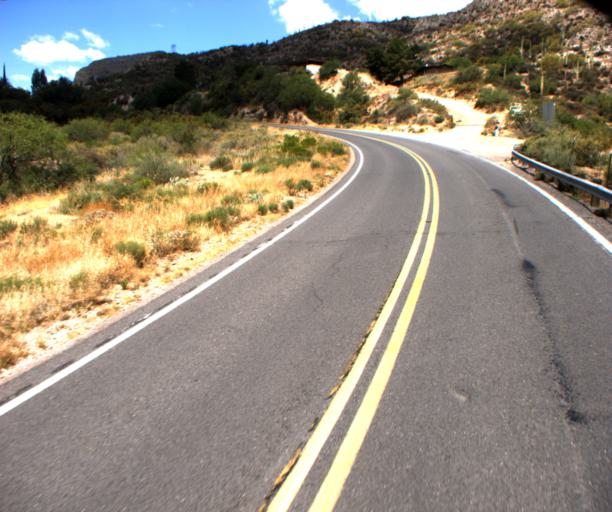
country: US
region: Arizona
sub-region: Pinal County
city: Superior
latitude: 33.1929
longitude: -111.0451
